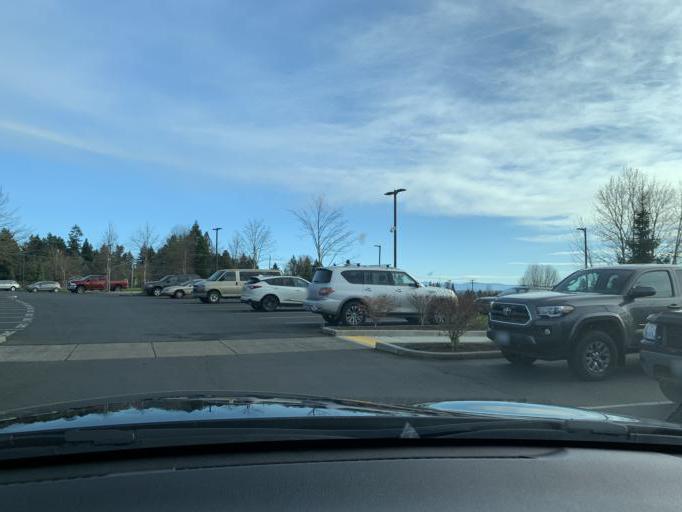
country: US
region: Washington
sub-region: Clark County
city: Mill Plain
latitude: 45.5937
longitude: -122.5058
